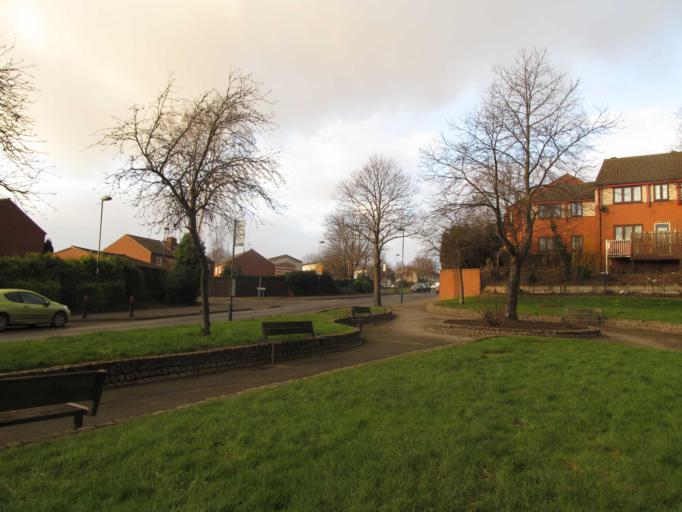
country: GB
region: England
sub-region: Nottingham
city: Nottingham
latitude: 52.9867
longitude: -1.1803
